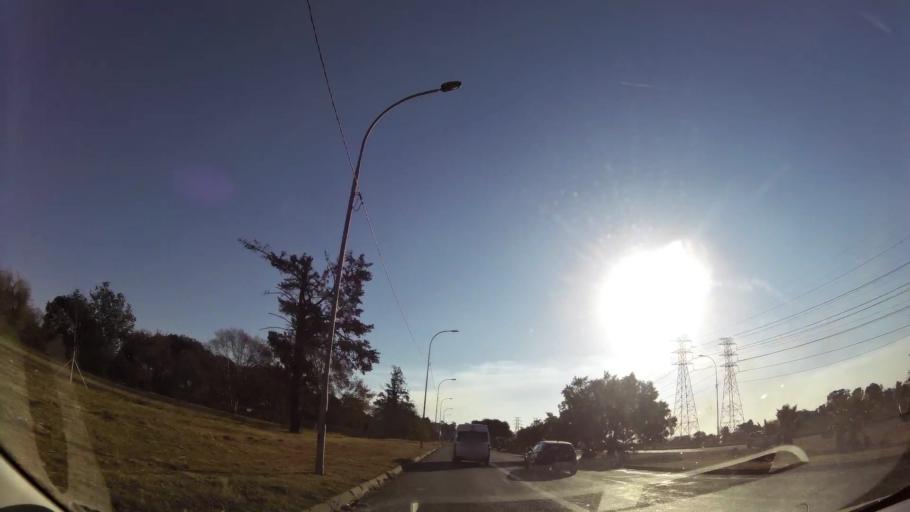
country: ZA
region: Gauteng
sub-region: City of Johannesburg Metropolitan Municipality
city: Roodepoort
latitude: -26.1831
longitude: 27.8958
